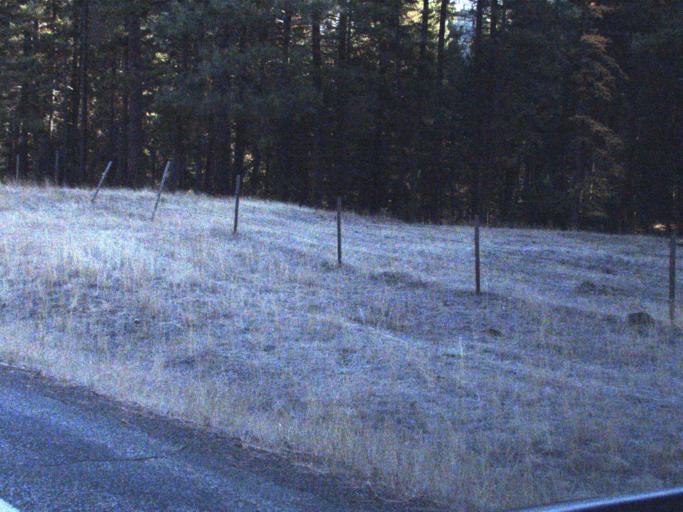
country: US
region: Washington
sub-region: Ferry County
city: Republic
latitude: 48.5952
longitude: -118.7401
